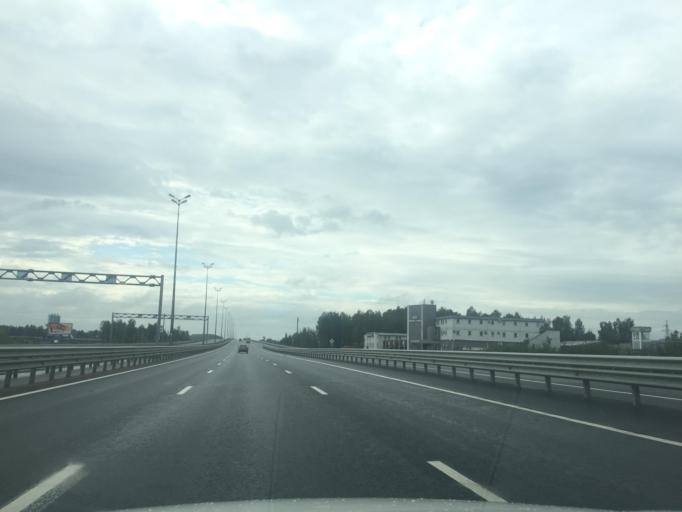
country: RU
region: Leningrad
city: Gatchina
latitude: 59.5601
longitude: 30.1660
